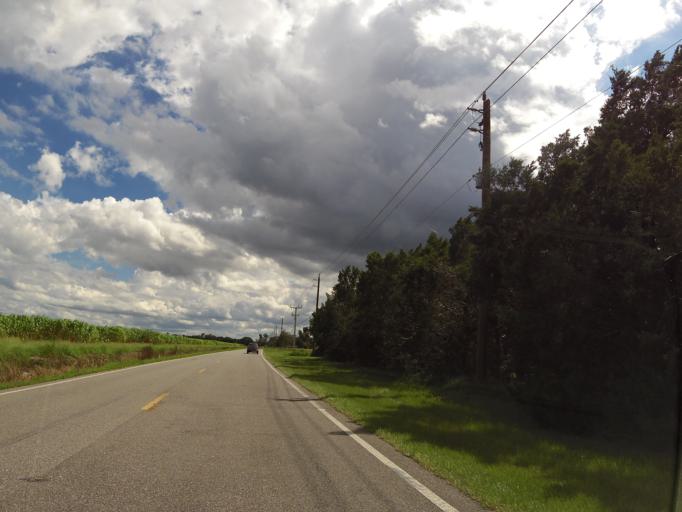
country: US
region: Florida
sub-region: Saint Johns County
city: Saint Augustine South
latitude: 29.8071
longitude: -81.4844
